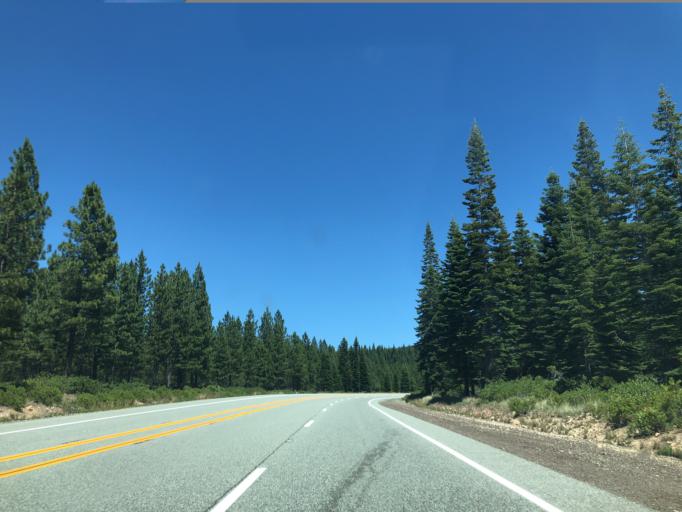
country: US
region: California
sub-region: Shasta County
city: Shingletown
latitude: 40.5408
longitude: -121.6069
